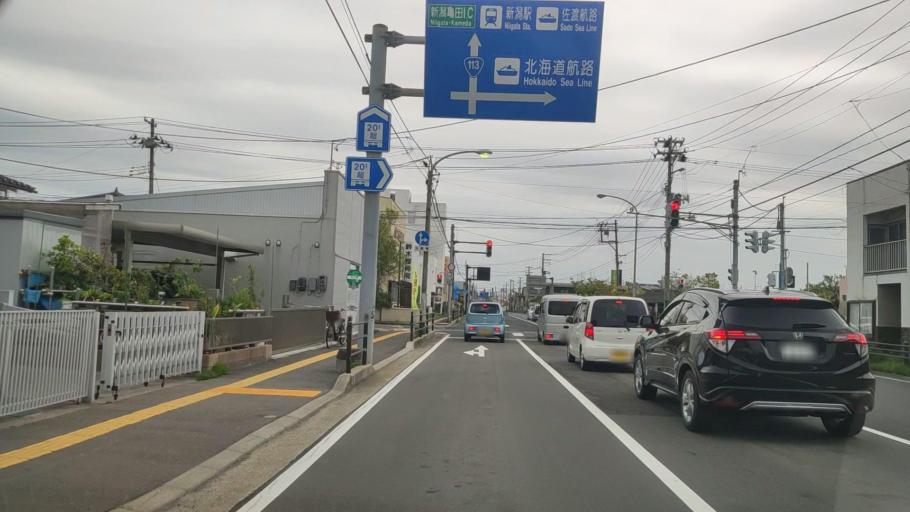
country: JP
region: Niigata
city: Niigata-shi
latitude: 37.9367
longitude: 139.0723
